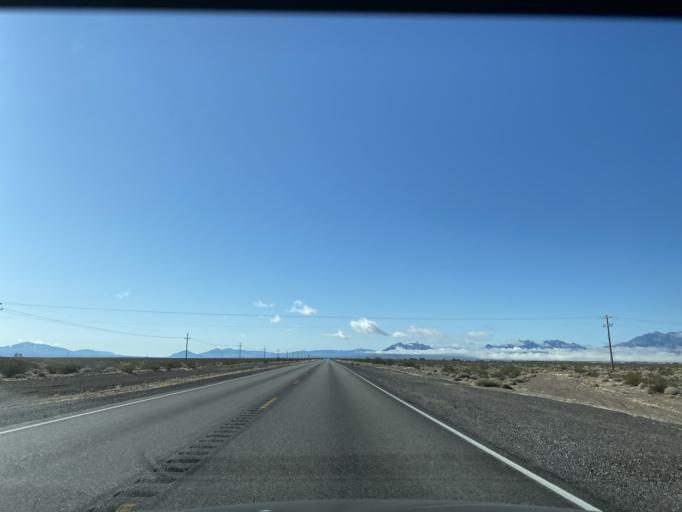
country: US
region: Nevada
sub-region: Nye County
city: Beatty
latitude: 36.5847
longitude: -116.4109
